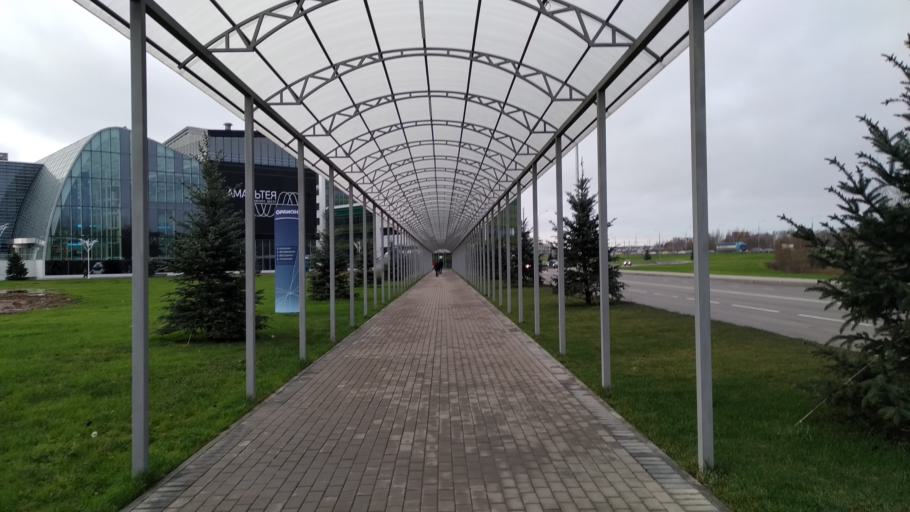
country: RU
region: Moskovskaya
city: Novoivanovskoye
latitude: 55.6977
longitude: 37.3476
